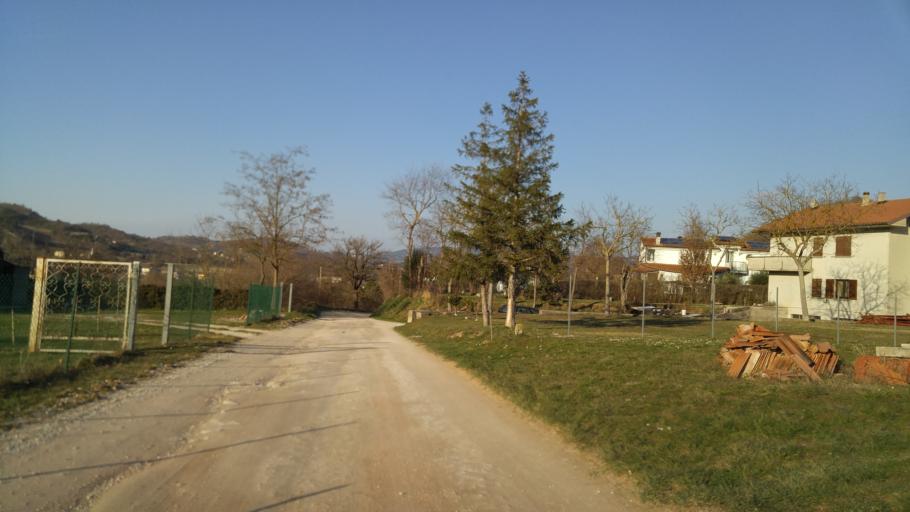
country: IT
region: The Marches
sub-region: Provincia di Pesaro e Urbino
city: Cagli
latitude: 43.5526
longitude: 12.6559
